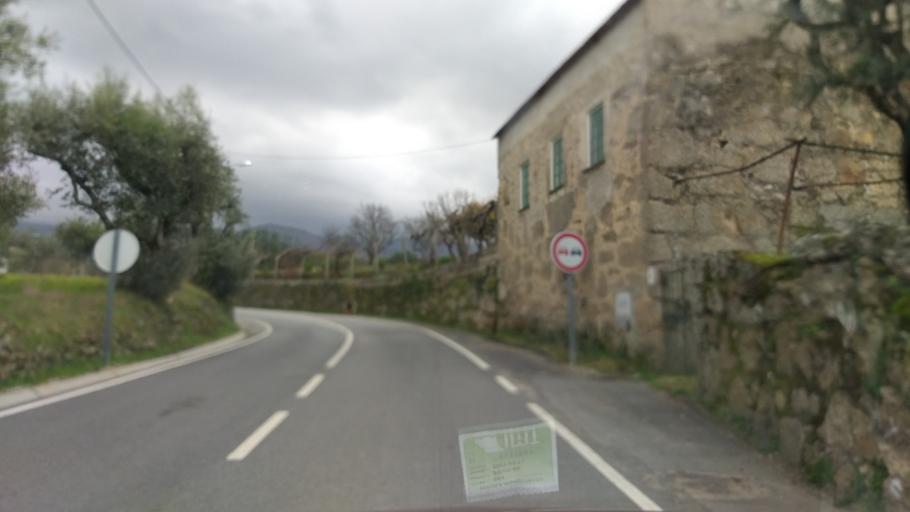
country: PT
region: Guarda
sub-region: Seia
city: Seia
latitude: 40.4733
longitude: -7.6369
